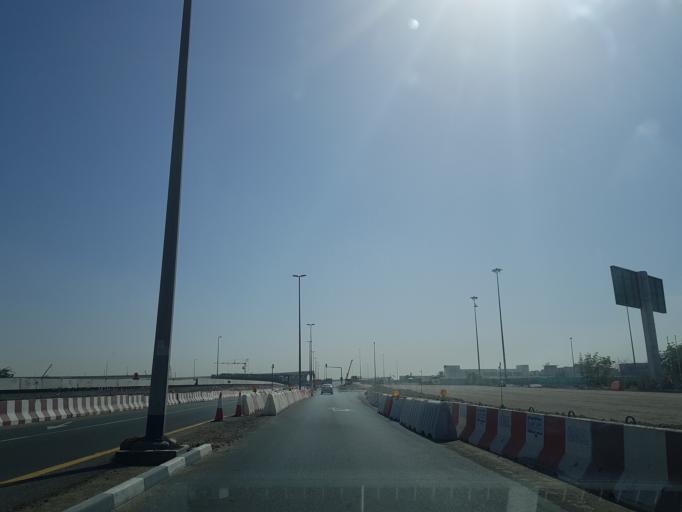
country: AE
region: Dubai
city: Dubai
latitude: 25.0165
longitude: 55.0876
